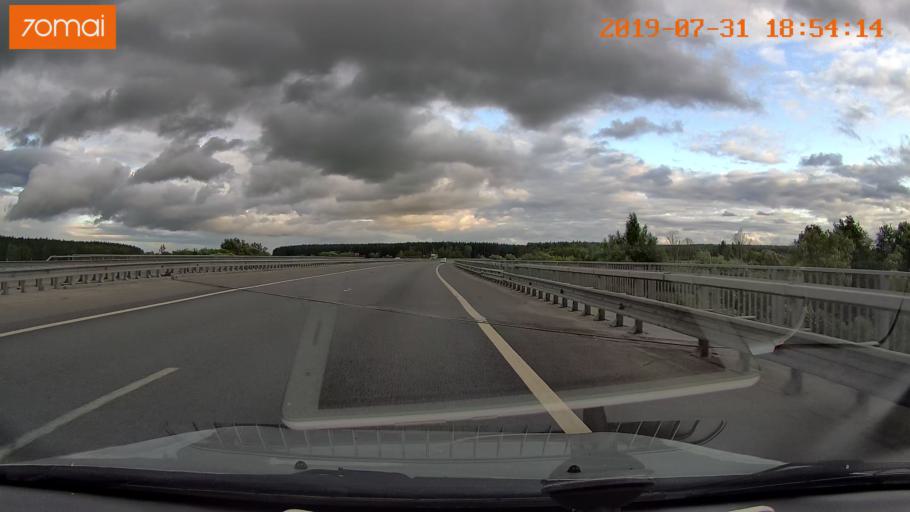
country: RU
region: Moskovskaya
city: Raduzhnyy
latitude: 55.1932
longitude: 38.6671
